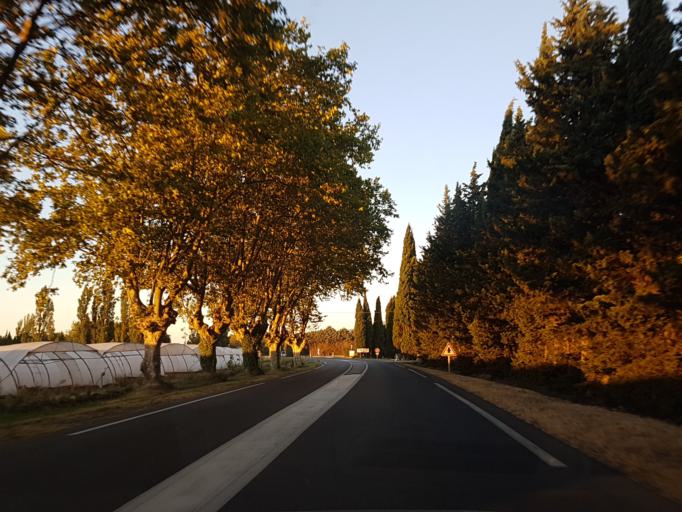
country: FR
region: Provence-Alpes-Cote d'Azur
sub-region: Departement du Vaucluse
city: Pernes-les-Fontaines
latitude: 44.0082
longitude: 5.0239
